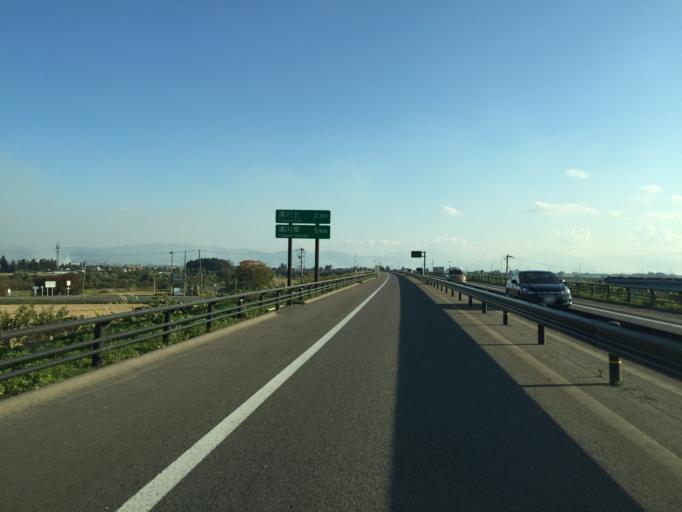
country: JP
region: Fukushima
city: Kitakata
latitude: 37.5945
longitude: 139.8770
